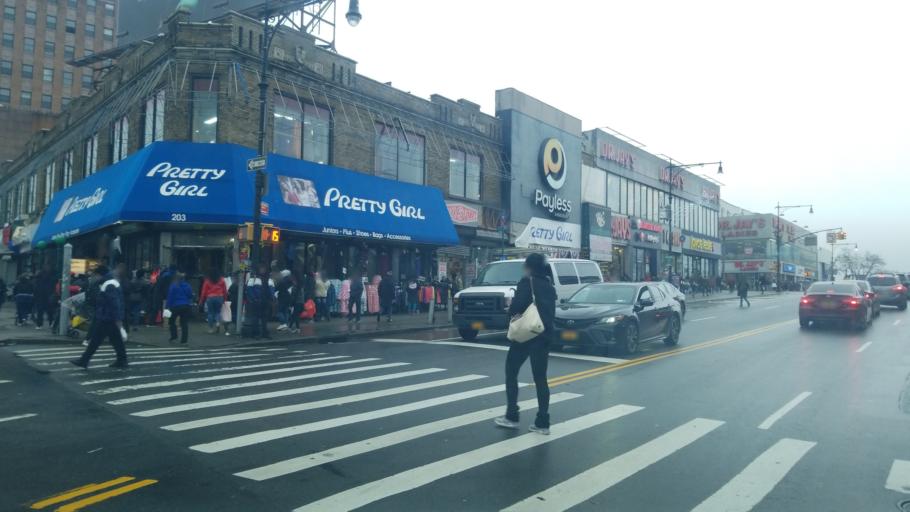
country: US
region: New York
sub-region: New York County
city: Inwood
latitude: 40.8624
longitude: -73.8969
